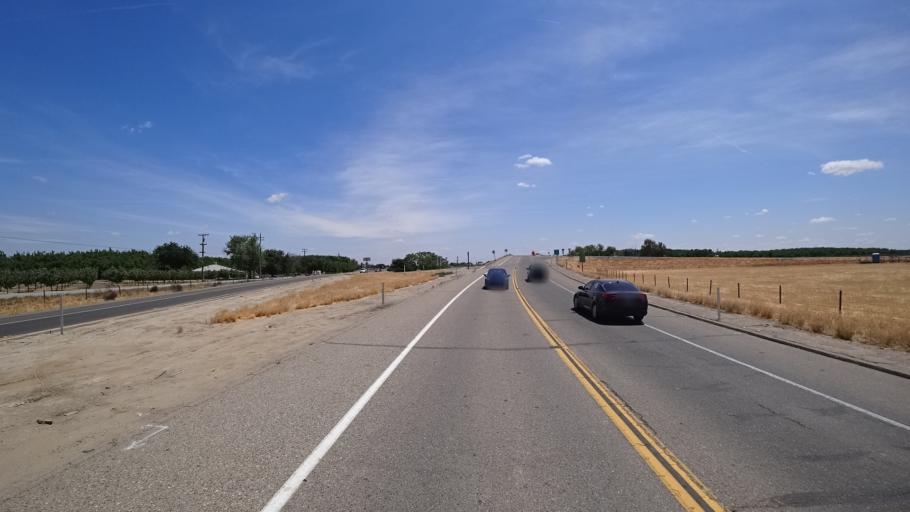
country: US
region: California
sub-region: Kings County
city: Lemoore
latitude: 36.2982
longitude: -119.7573
